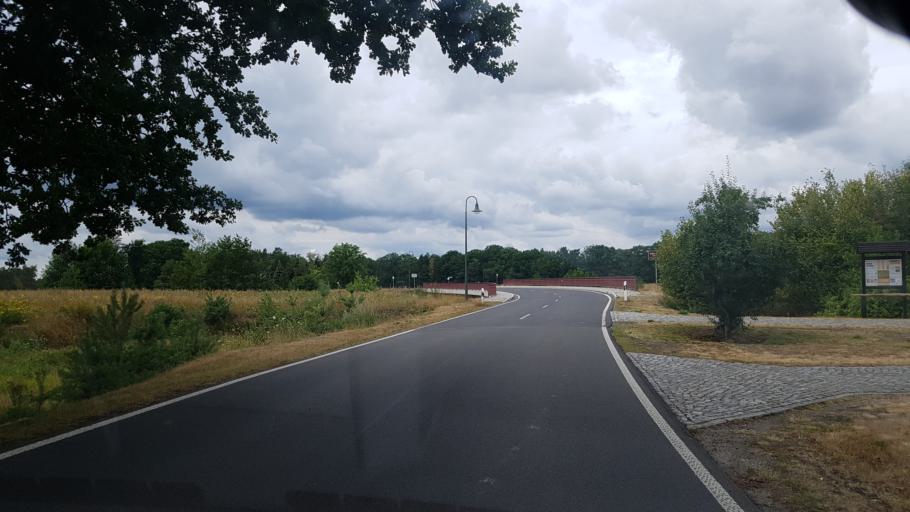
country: DE
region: Saxony
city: Mucka
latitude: 51.3771
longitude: 14.7151
